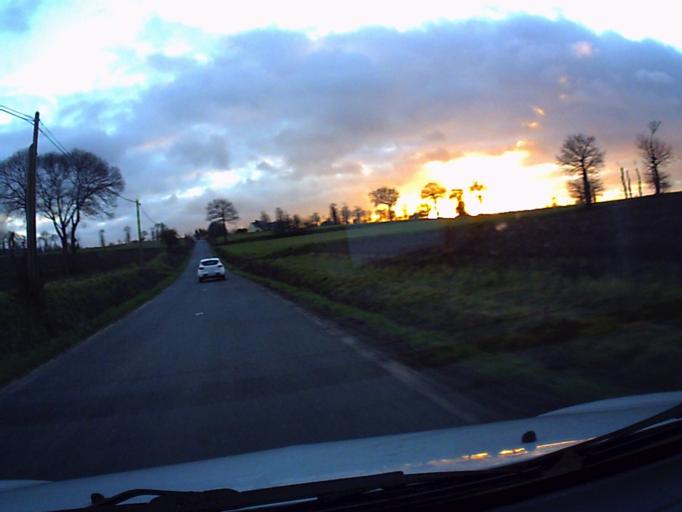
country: FR
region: Brittany
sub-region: Departement d'Ille-et-Vilaine
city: Iffendic
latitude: 48.1357
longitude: -2.0265
